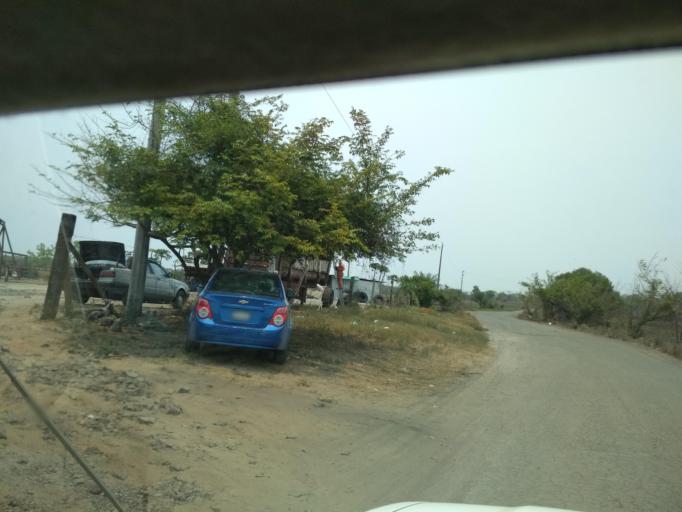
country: MX
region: Veracruz
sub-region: Veracruz
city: Delfino Victoria (Santa Fe)
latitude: 19.2012
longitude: -96.2608
